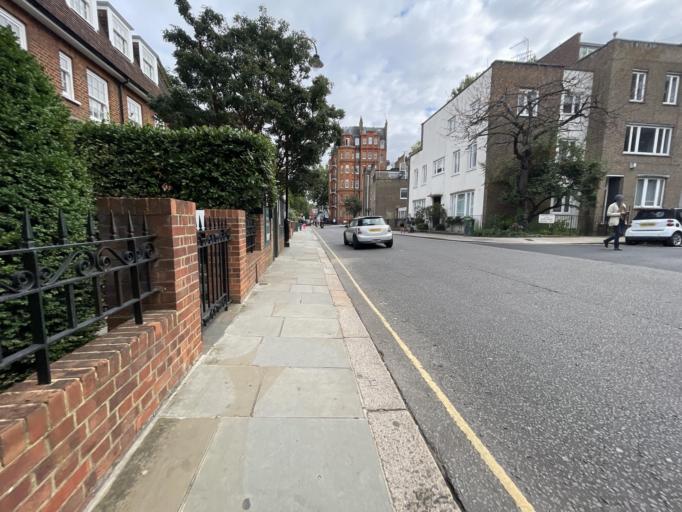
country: GB
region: England
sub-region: Greater London
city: Chelsea
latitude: 51.4921
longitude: -0.1808
